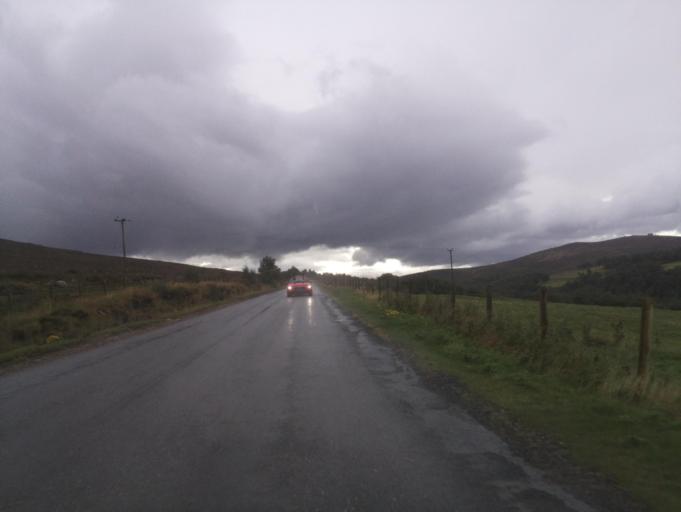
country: GB
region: Scotland
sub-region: Highland
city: Grantown on Spey
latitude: 57.2946
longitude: -3.5529
